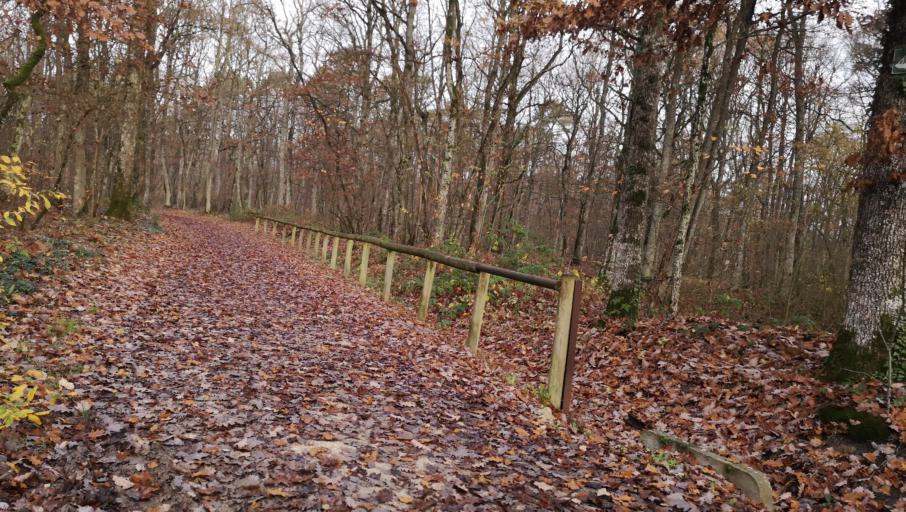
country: FR
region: Centre
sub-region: Departement du Loiret
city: Semoy
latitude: 47.9393
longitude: 1.9714
